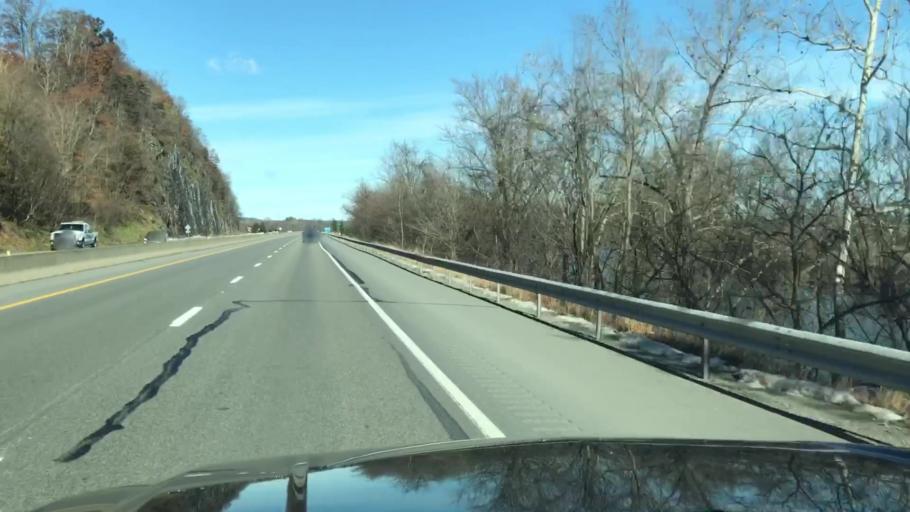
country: US
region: Pennsylvania
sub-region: Snyder County
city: Selinsgrove
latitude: 40.7620
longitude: -76.8646
